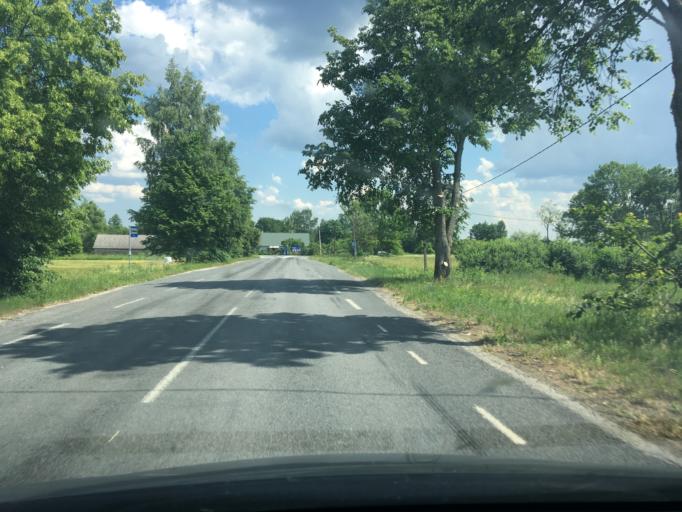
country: EE
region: Paernumaa
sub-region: Halinga vald
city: Parnu-Jaagupi
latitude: 58.7074
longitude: 24.3995
